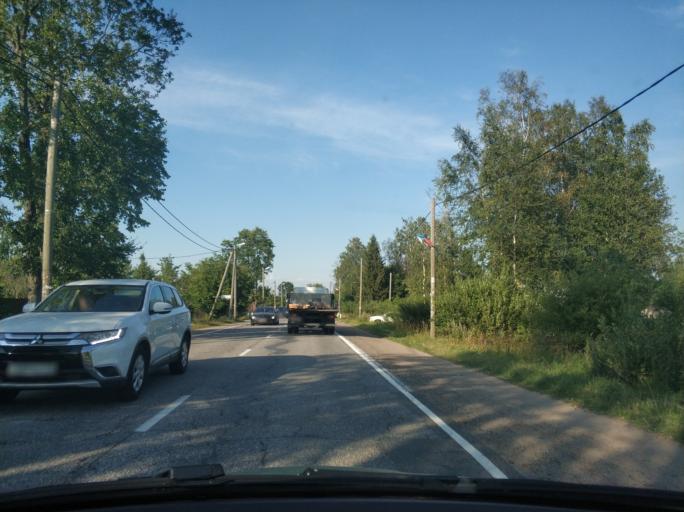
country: RU
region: Leningrad
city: Borisova Griva
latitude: 60.0932
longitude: 30.9623
